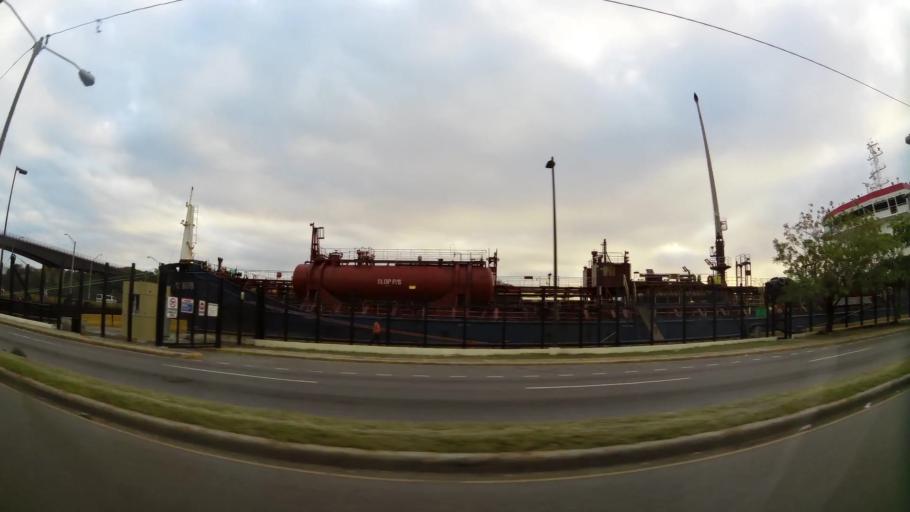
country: DO
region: Nacional
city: San Carlos
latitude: 18.4786
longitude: -69.8825
